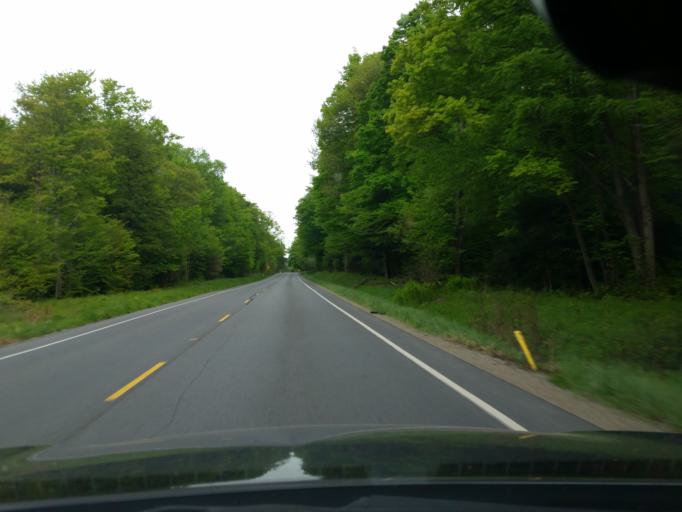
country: US
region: Pennsylvania
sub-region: McKean County
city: Kane
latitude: 41.5758
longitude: -78.9209
